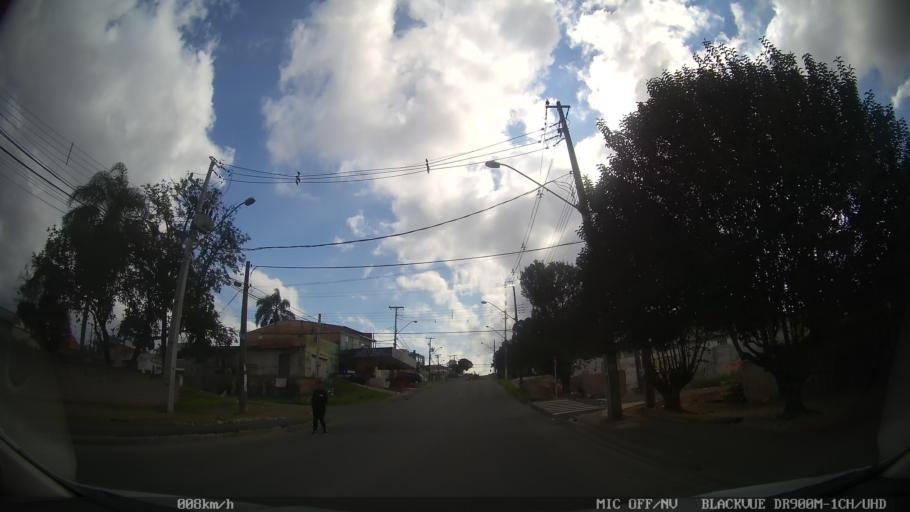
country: BR
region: Parana
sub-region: Pinhais
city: Pinhais
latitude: -25.3654
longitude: -49.1883
